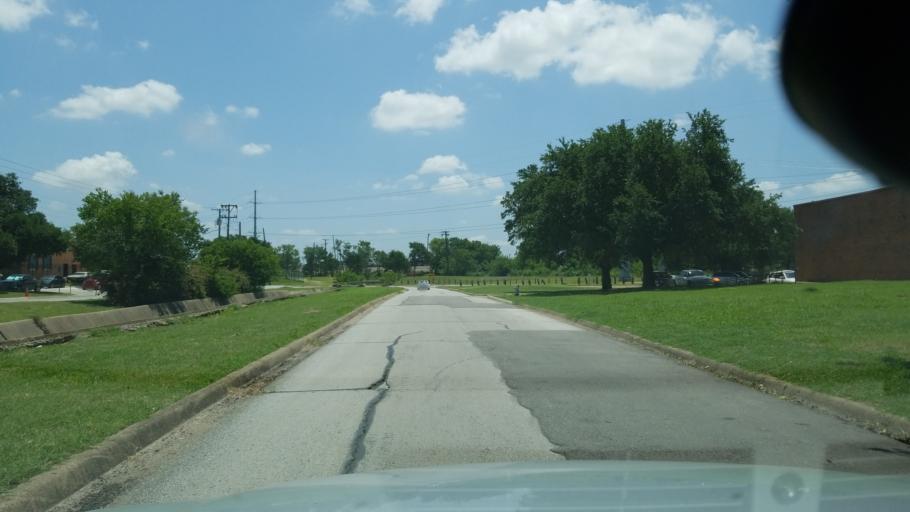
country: US
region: Texas
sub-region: Dallas County
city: Irving
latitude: 32.8149
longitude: -96.8817
